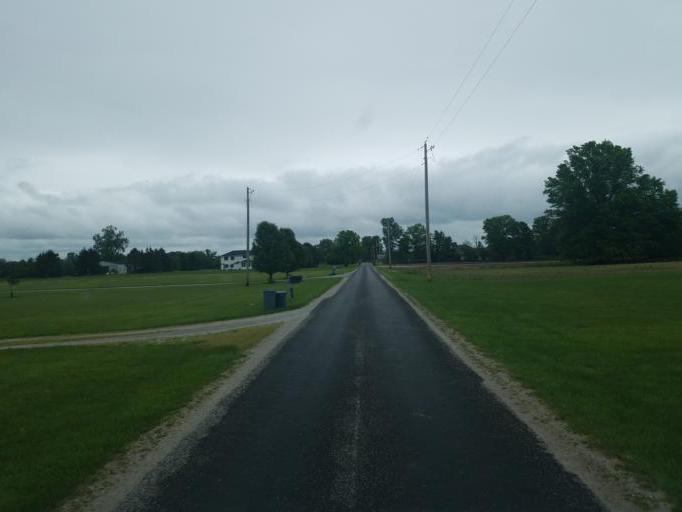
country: US
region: Ohio
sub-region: Marion County
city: Marion
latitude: 40.5386
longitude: -83.0144
